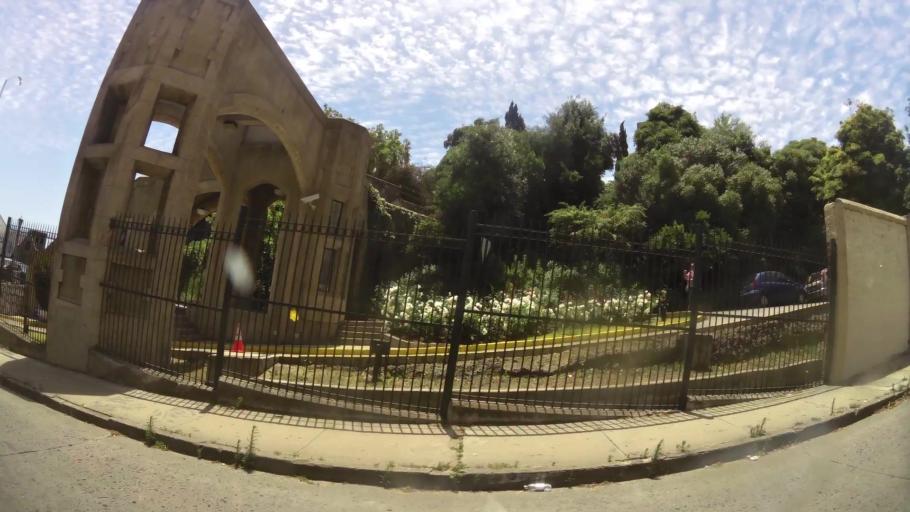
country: CL
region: Valparaiso
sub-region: Provincia de Valparaiso
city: Valparaiso
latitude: -33.0356
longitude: -71.5971
